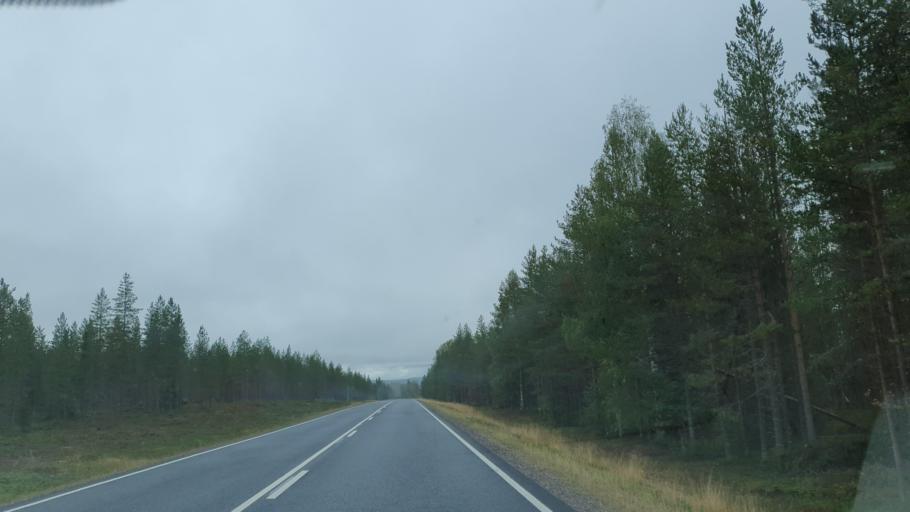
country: FI
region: Northern Ostrobothnia
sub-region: Oulunkaari
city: Pudasjaervi
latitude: 65.3401
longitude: 27.4206
